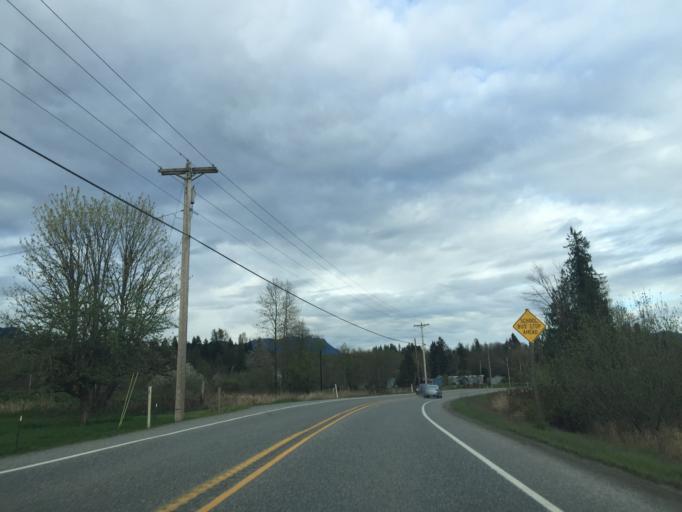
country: US
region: Washington
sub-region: Snohomish County
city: Arlington Heights
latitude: 48.2737
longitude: -121.9868
